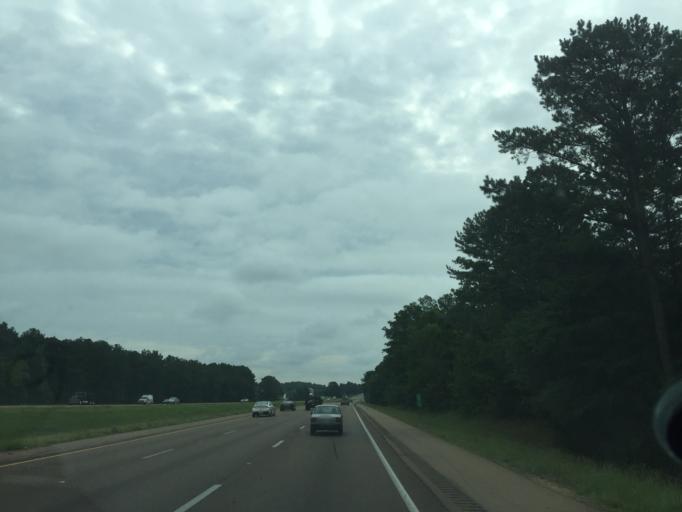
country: US
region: Mississippi
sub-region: Rankin County
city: Pearl
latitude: 32.2670
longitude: -90.0977
